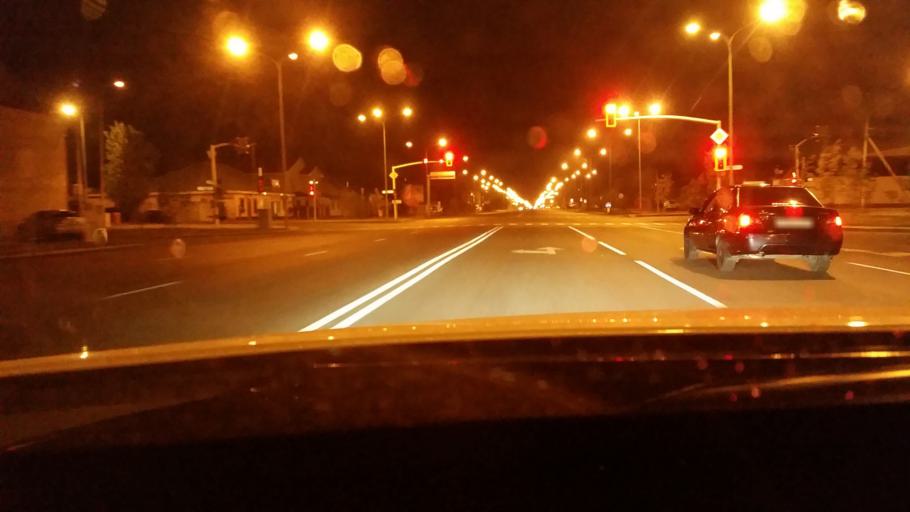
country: KZ
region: Astana Qalasy
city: Astana
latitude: 51.1335
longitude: 71.4941
